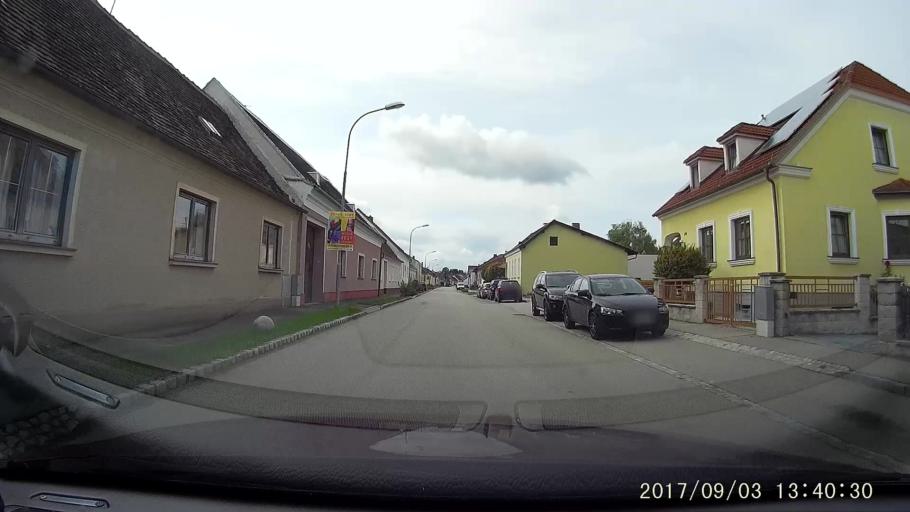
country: AT
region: Lower Austria
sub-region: Politischer Bezirk Hollabrunn
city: Wullersdorf
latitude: 48.6001
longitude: 16.0681
